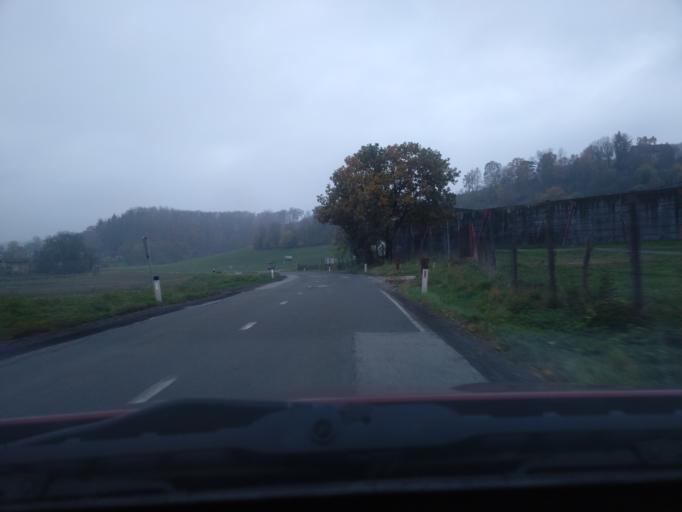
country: SI
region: Pesnica
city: Pesnica pri Mariboru
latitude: 46.6003
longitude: 15.6560
